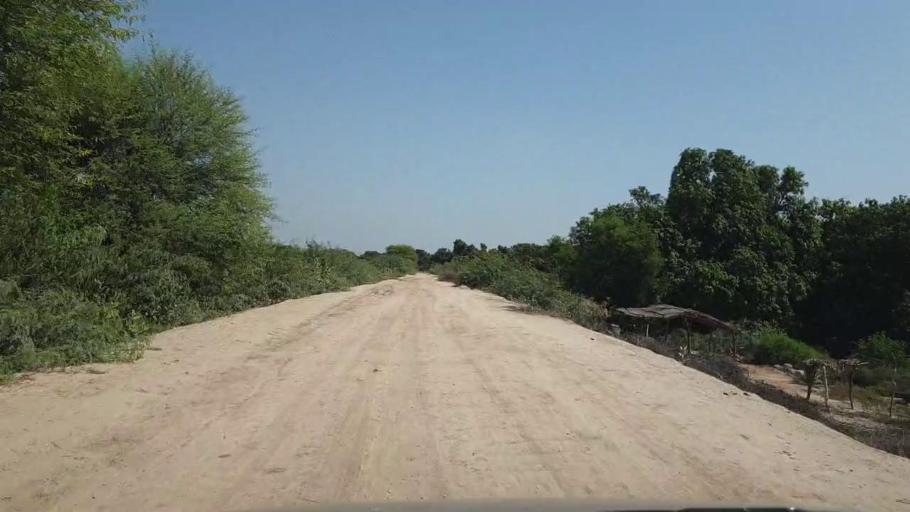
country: PK
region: Sindh
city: Matiari
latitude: 25.6267
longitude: 68.4790
